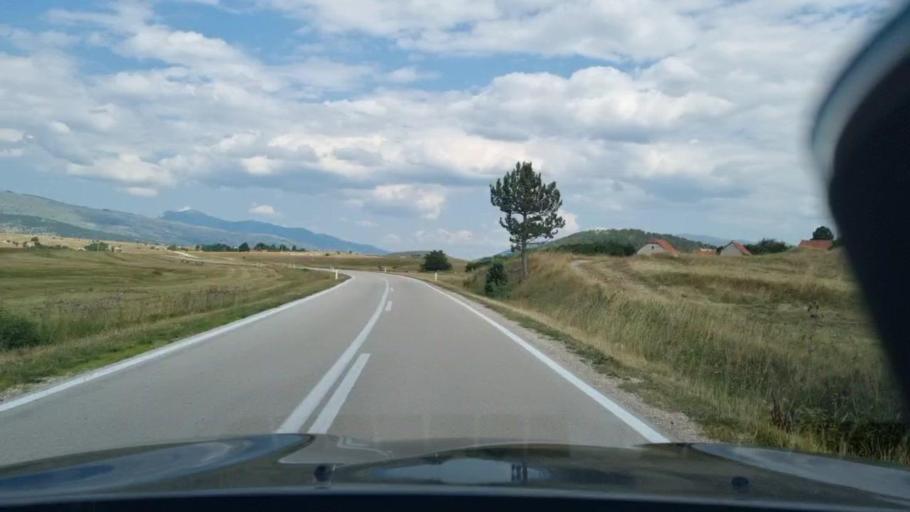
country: BA
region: Federation of Bosnia and Herzegovina
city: Bosansko Grahovo
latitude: 44.1586
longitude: 16.3918
